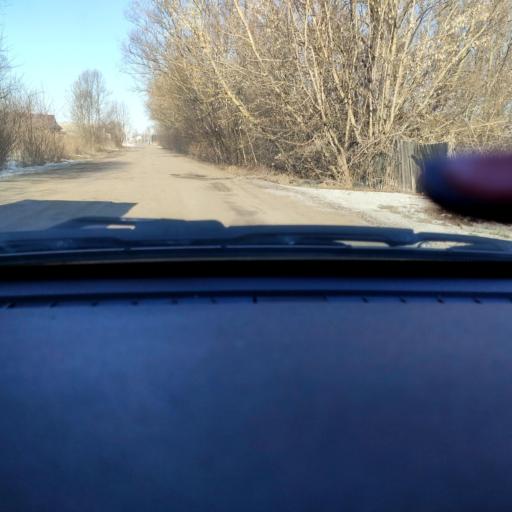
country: RU
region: Voronezj
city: Latnaya
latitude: 51.6945
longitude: 38.9456
